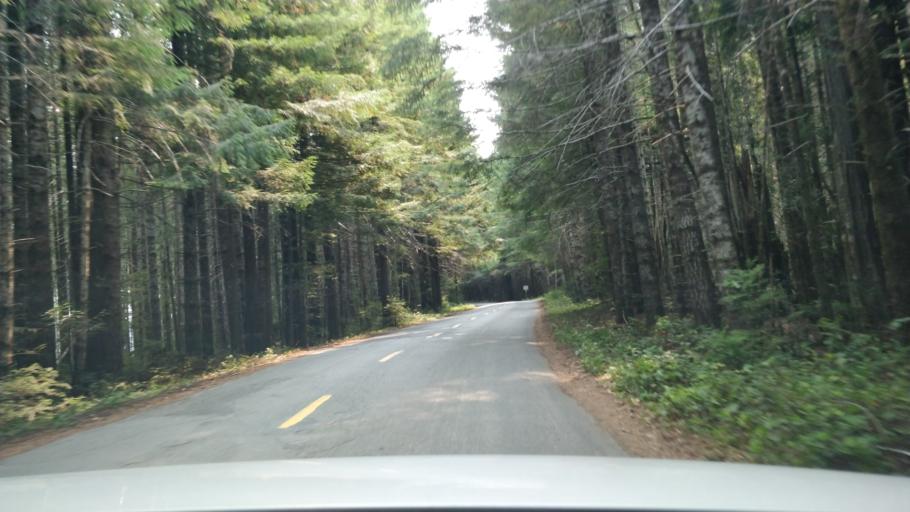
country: US
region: California
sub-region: Humboldt County
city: Westhaven-Moonstone
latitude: 41.2477
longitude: -123.9829
